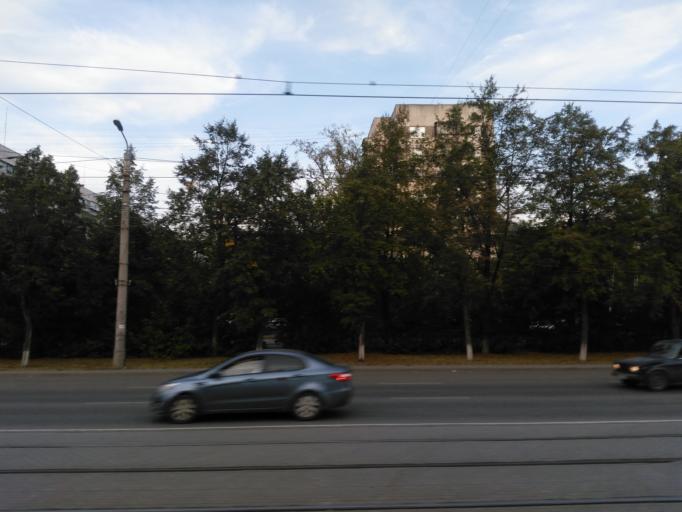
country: RU
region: Chelyabinsk
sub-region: Gorod Chelyabinsk
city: Chelyabinsk
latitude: 55.1760
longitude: 61.3995
